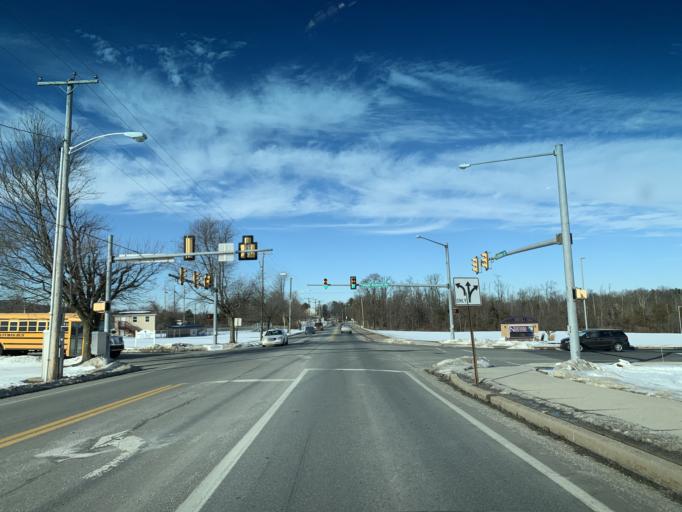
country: US
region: Pennsylvania
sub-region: York County
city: Dillsburg
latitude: 40.0958
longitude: -77.0310
